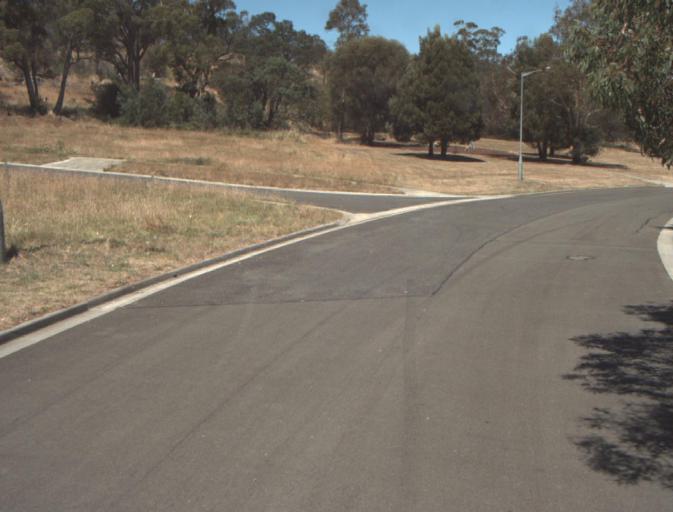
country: AU
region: Tasmania
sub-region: Launceston
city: Mayfield
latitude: -41.3768
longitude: 147.1391
